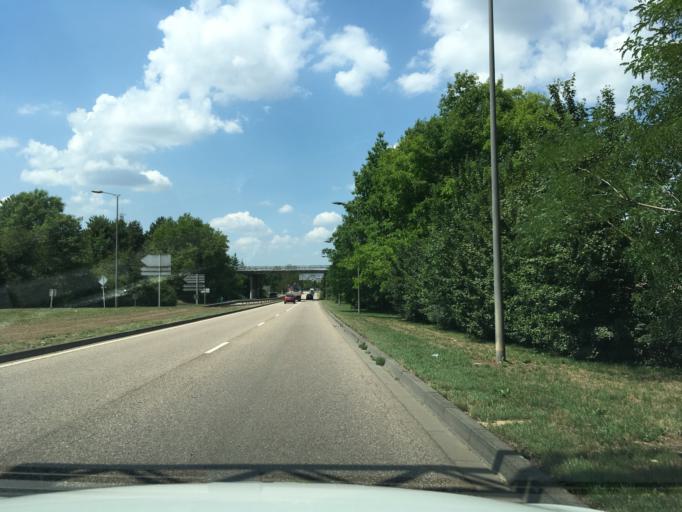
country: FR
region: Lorraine
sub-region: Departement de la Moselle
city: Saint-Julien-les-Metz
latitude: 49.1195
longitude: 6.2277
